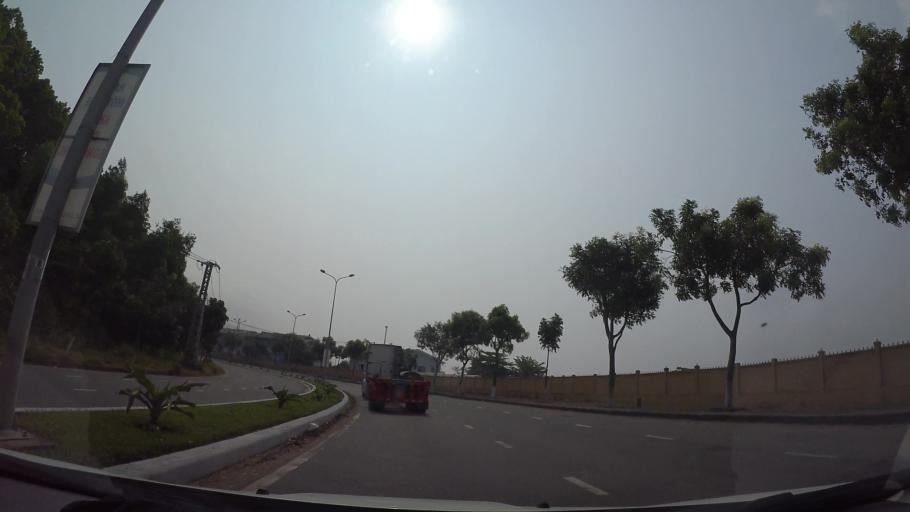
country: VN
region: Da Nang
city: Da Nang
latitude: 16.1177
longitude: 108.2253
